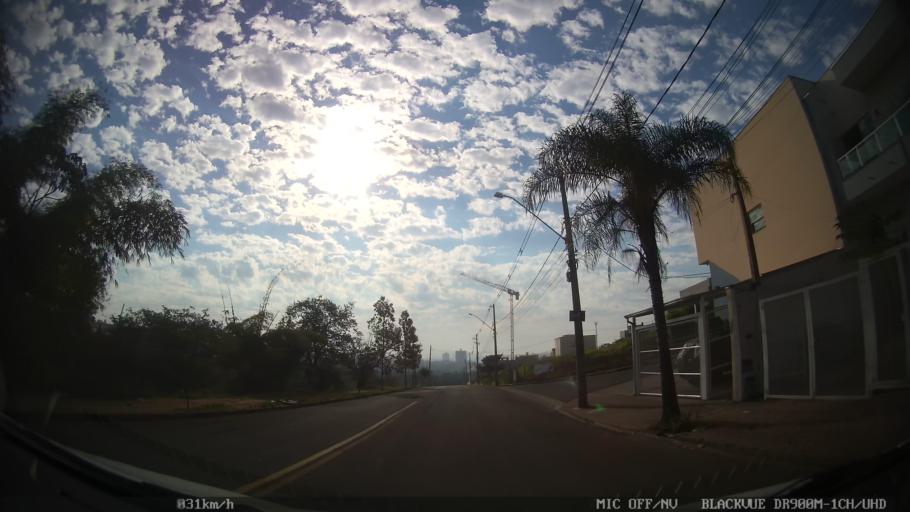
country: BR
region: Sao Paulo
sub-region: Americana
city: Americana
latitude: -22.7381
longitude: -47.3498
